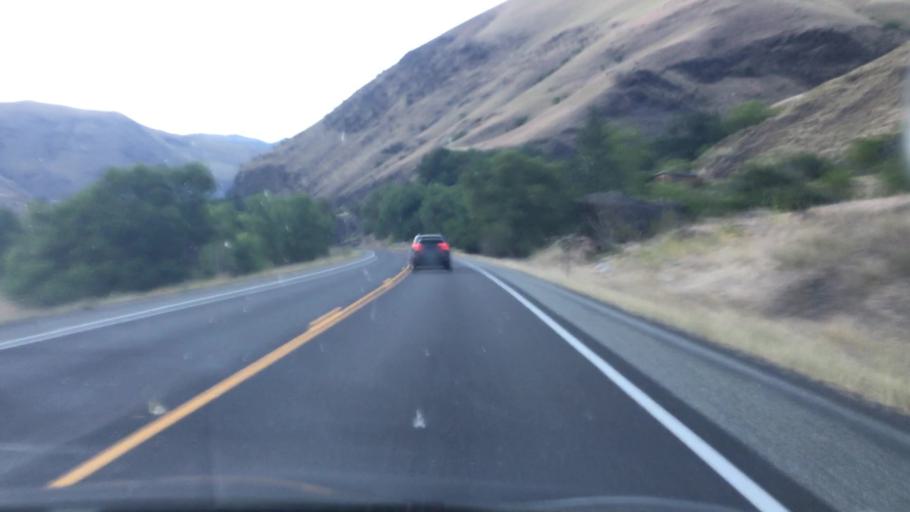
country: US
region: Idaho
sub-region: Valley County
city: McCall
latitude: 45.3395
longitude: -116.3481
